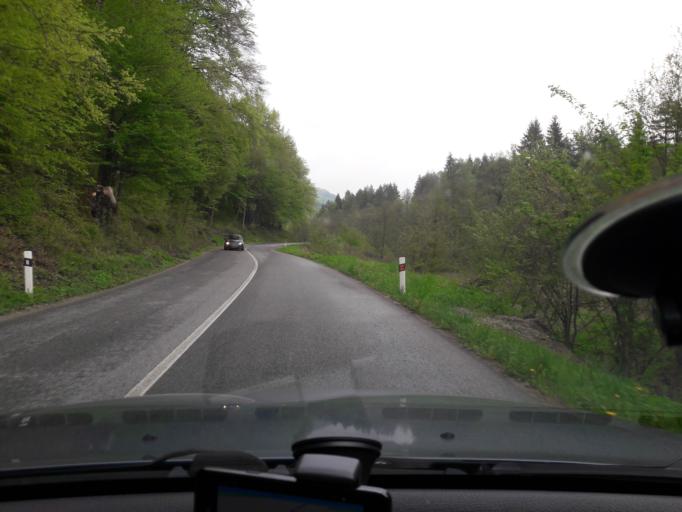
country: SK
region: Banskobystricky
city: Tisovec
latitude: 48.7186
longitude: 20.0066
